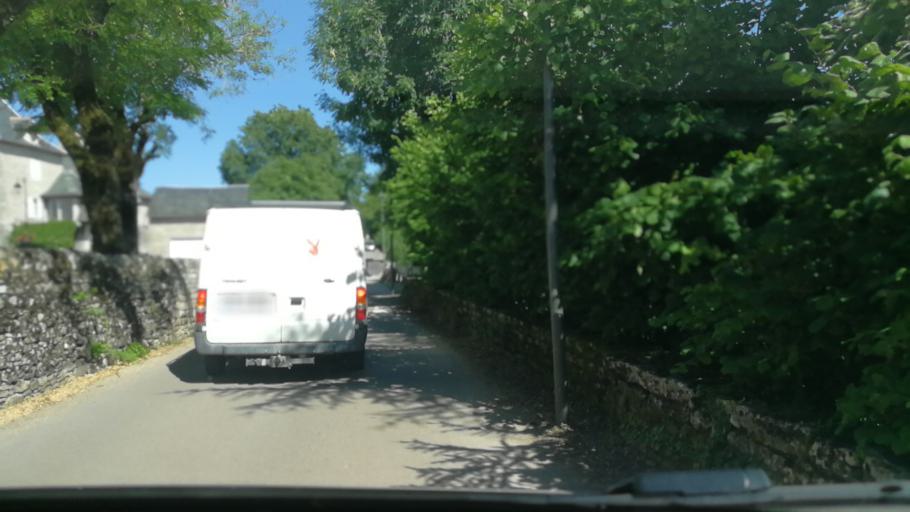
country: FR
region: Midi-Pyrenees
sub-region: Departement de l'Aveyron
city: Sebazac-Concoures
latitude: 44.4195
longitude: 2.5634
